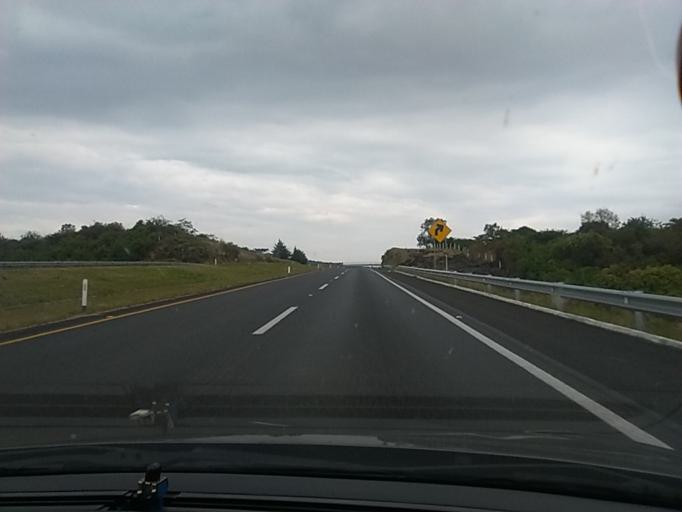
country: MX
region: Michoacan
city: Penjamillo de Degollado
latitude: 20.0304
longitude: -101.9215
